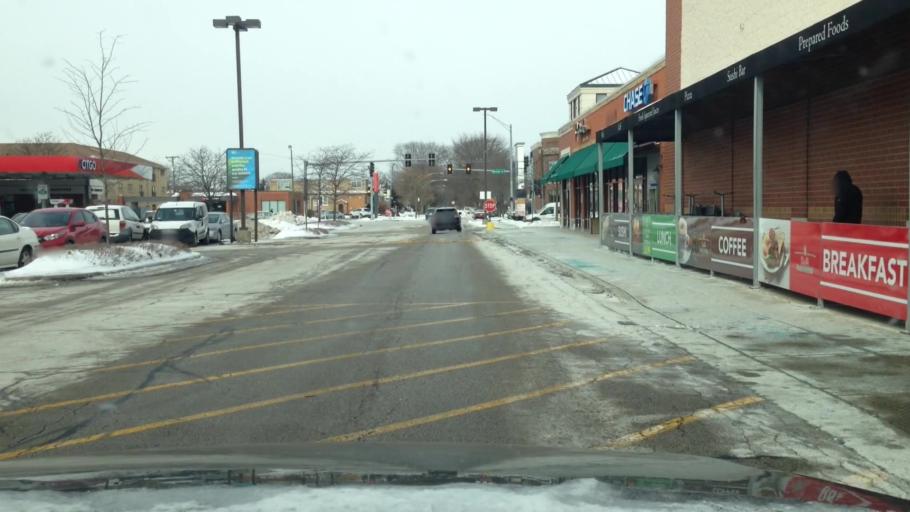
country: US
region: Illinois
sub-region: Cook County
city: River Grove
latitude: 41.9366
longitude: -87.8336
